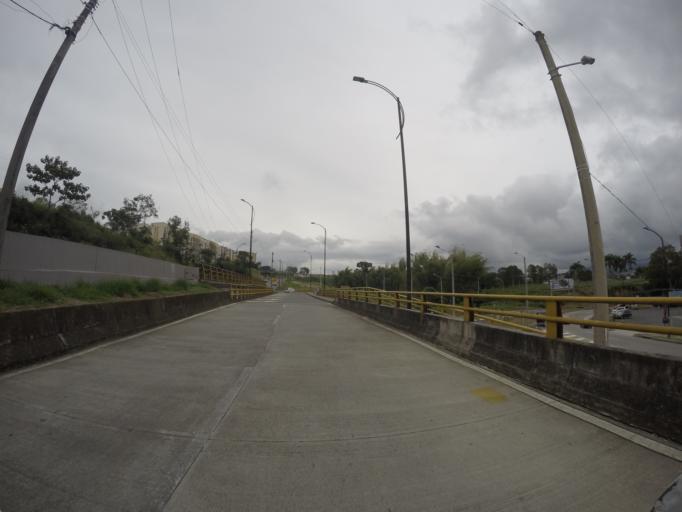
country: CO
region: Risaralda
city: Pereira
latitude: 4.8096
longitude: -75.7344
